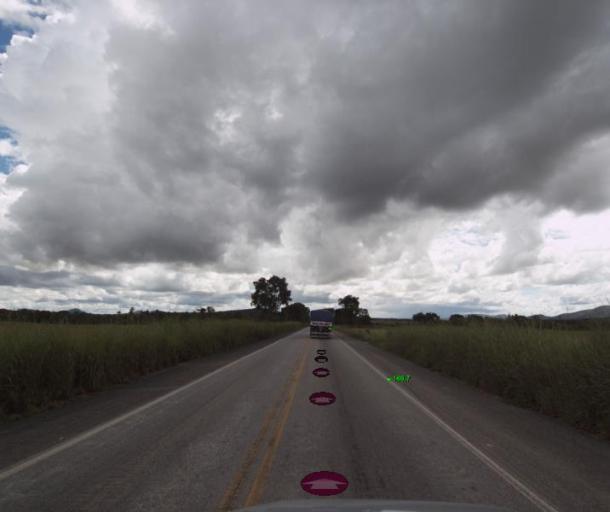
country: BR
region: Goias
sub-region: Uruacu
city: Uruacu
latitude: -14.2585
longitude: -49.1418
